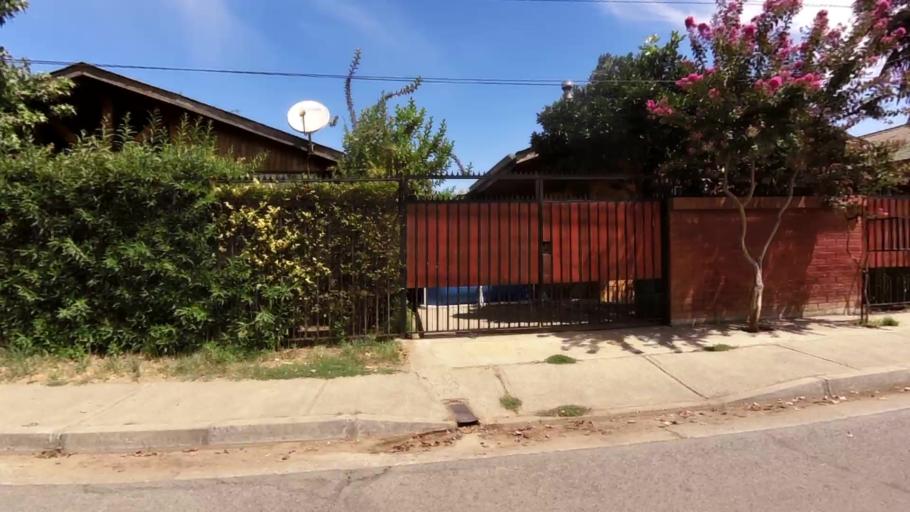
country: CL
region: O'Higgins
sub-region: Provincia de Cachapoal
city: Graneros
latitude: -34.0668
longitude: -70.7213
